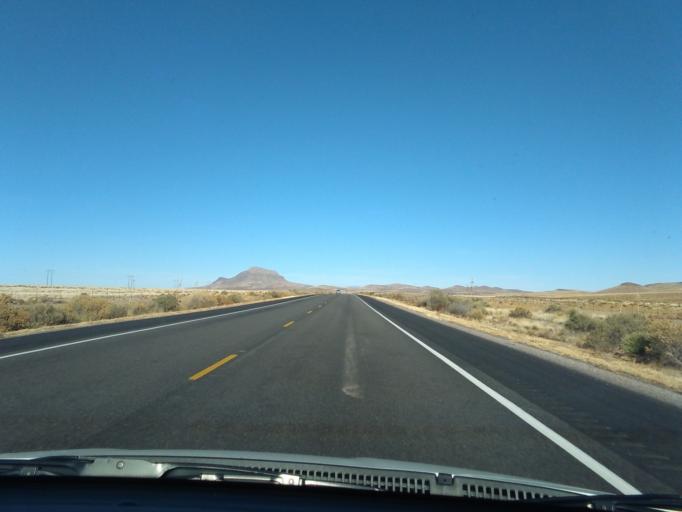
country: US
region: New Mexico
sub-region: Dona Ana County
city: Hatch
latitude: 32.5403
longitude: -107.4834
